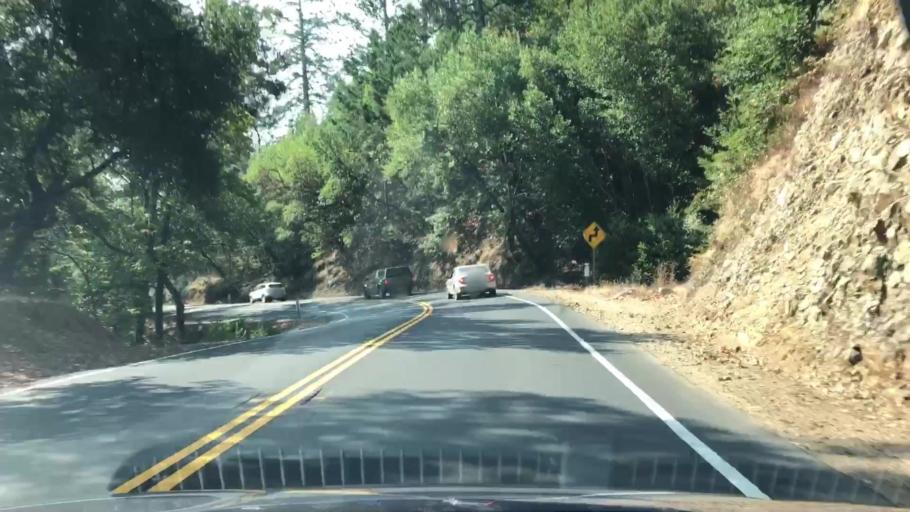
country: US
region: California
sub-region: Napa County
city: Calistoga
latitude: 38.6218
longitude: -122.5979
